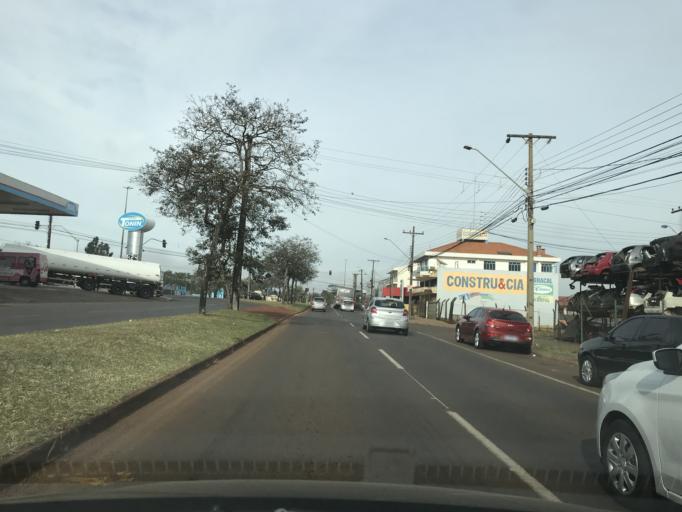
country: BR
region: Parana
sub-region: Cascavel
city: Cascavel
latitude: -24.9672
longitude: -53.4842
